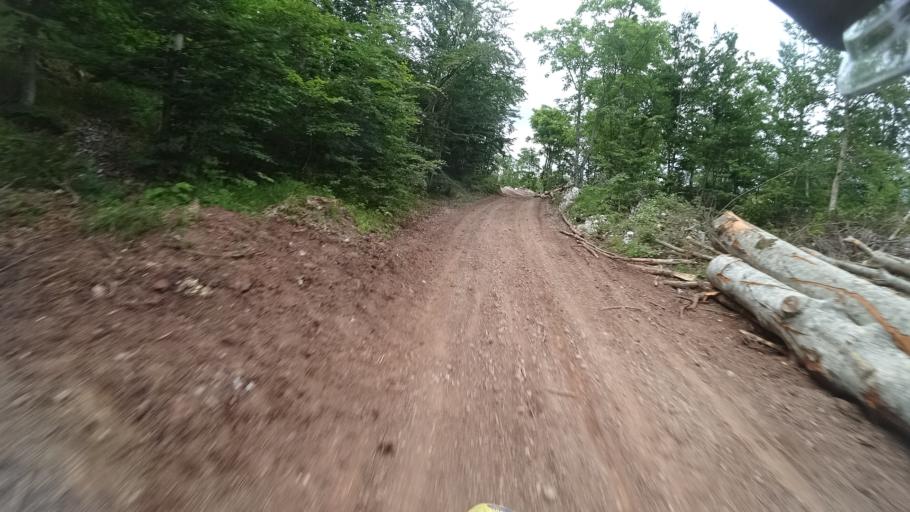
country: HR
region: Zadarska
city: Obrovac
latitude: 44.2898
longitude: 15.6747
